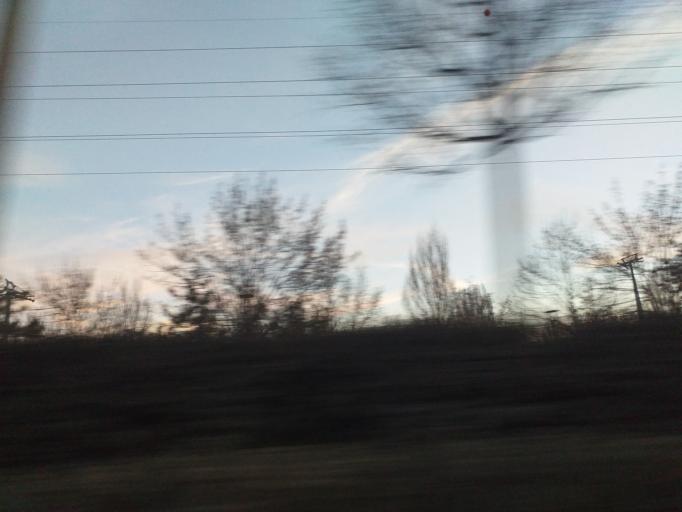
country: TR
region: Ankara
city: Ankara
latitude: 39.9540
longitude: 32.8147
